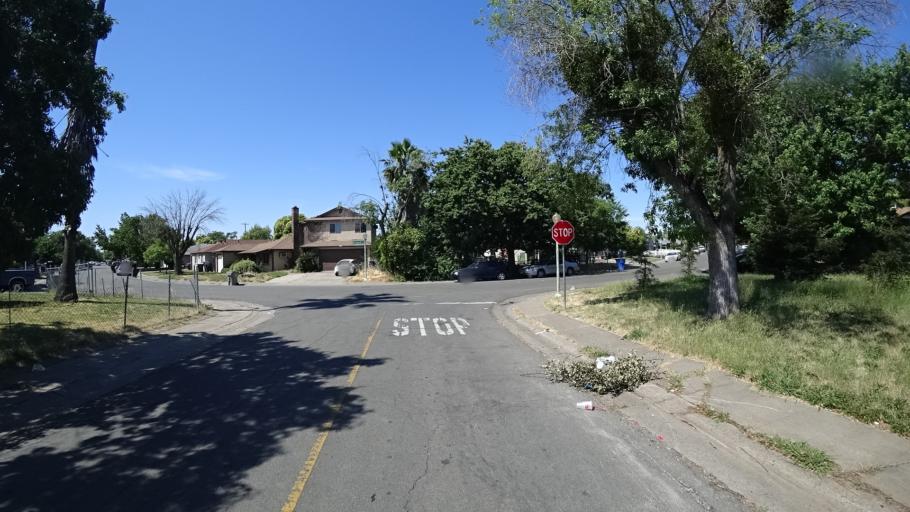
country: US
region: California
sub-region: Sacramento County
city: Florin
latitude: 38.5292
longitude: -121.4160
